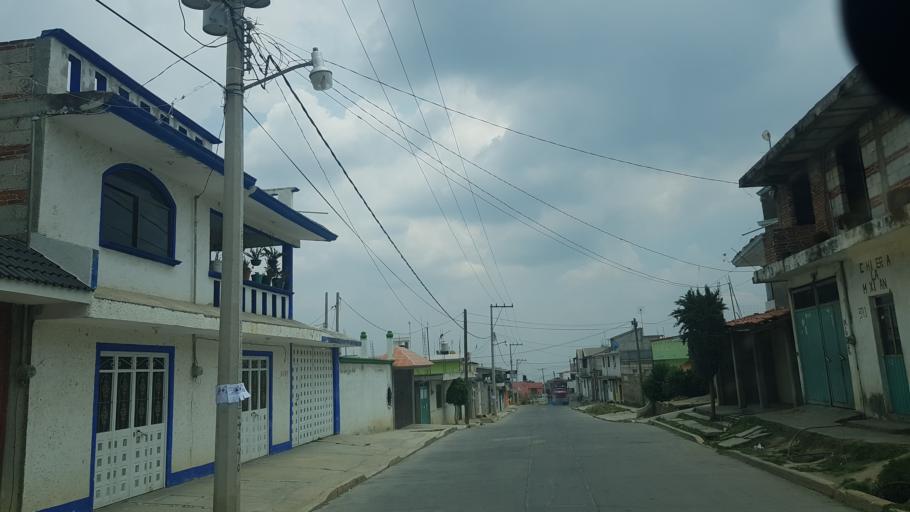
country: MX
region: Puebla
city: Domingo Arenas
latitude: 19.1508
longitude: -98.4964
